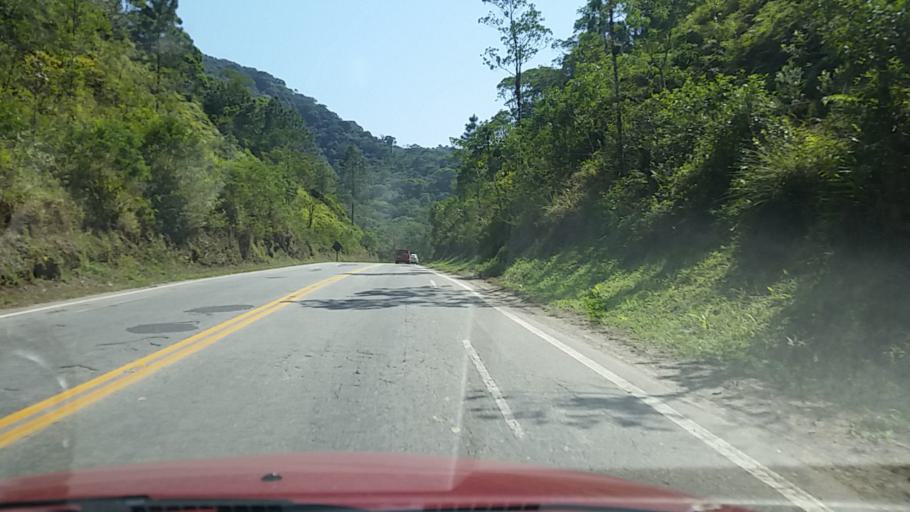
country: BR
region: Sao Paulo
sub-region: Miracatu
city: Miracatu
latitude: -24.3701
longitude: -47.4936
